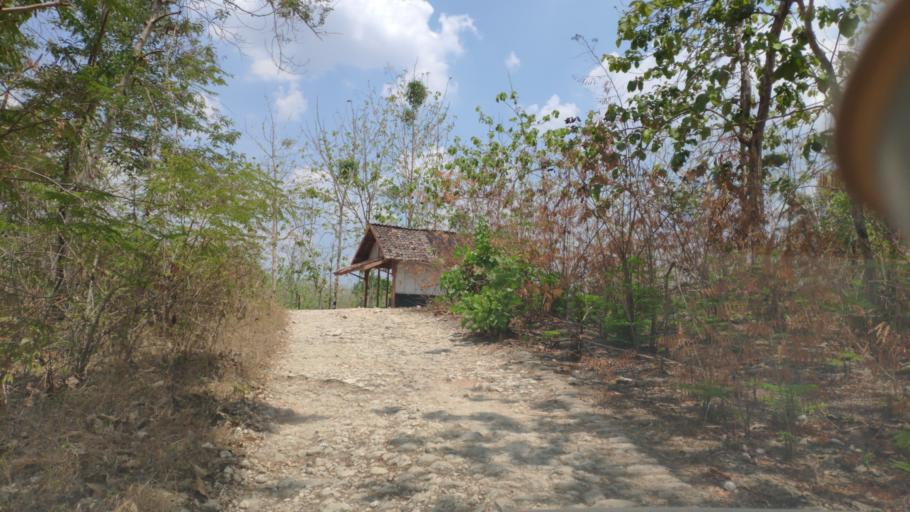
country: ID
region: Central Java
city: Suruhan
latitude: -6.9960
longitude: 111.5198
